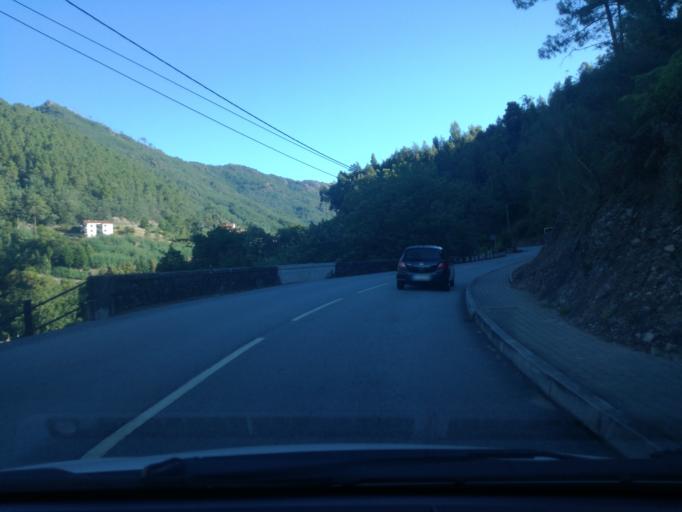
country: PT
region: Braga
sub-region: Vieira do Minho
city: Real
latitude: 41.7199
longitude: -8.1641
